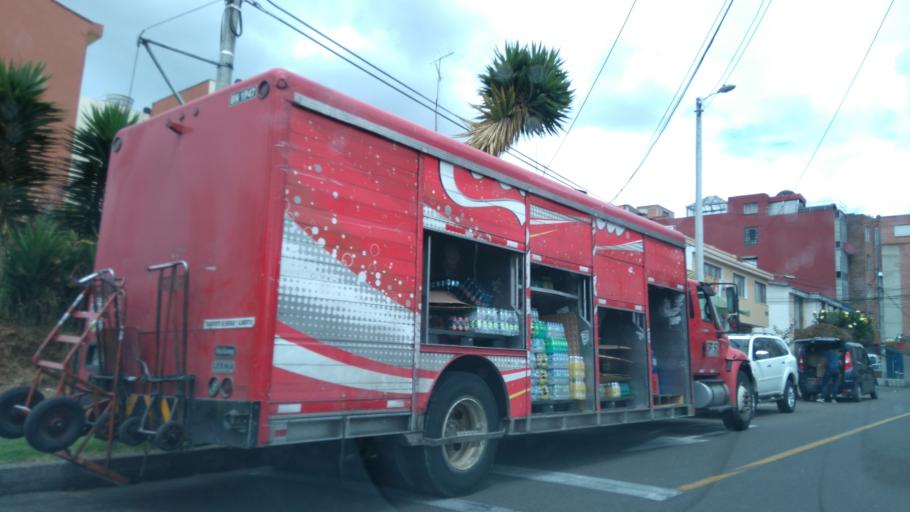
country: CO
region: Bogota D.C.
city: Barrio San Luis
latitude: 4.6709
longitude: -74.0617
